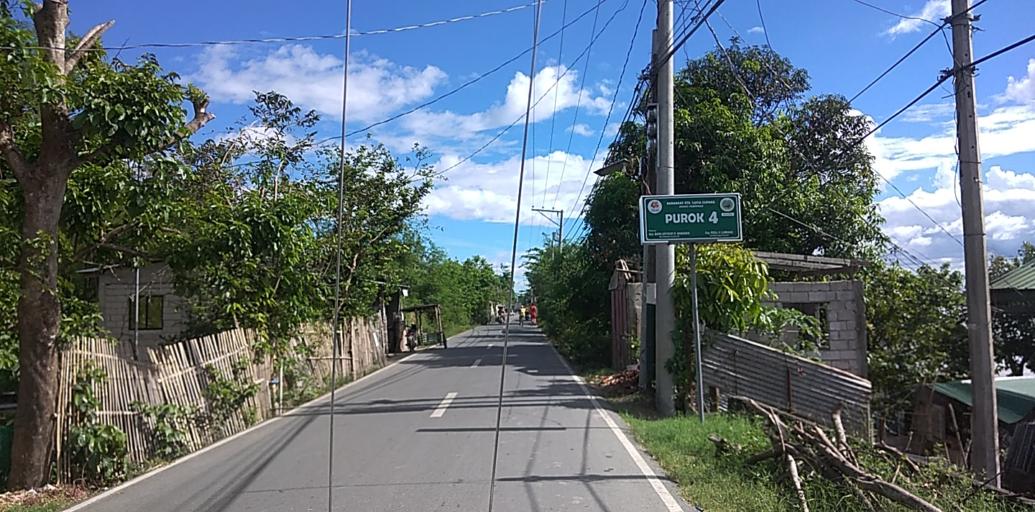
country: PH
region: Central Luzon
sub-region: Province of Pampanga
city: Arayat
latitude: 15.1365
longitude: 120.7852
